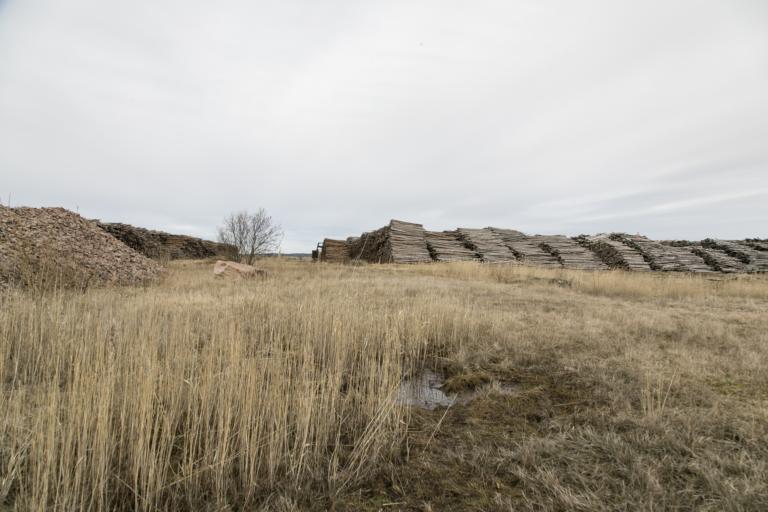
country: SE
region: Halland
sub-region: Varbergs Kommun
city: Varberg
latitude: 57.1187
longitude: 12.2378
